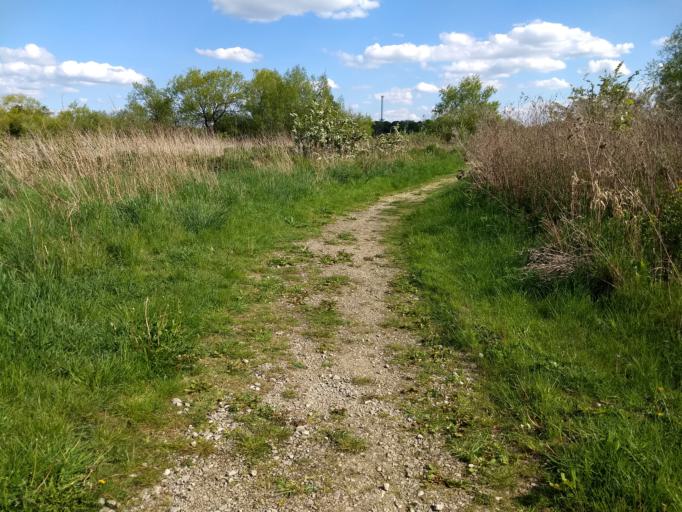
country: GB
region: England
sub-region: Milton Keynes
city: Castlethorpe
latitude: 52.0730
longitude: -0.8246
